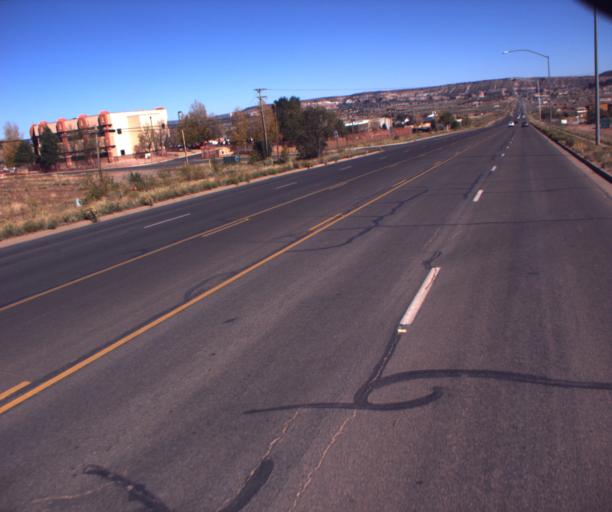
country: US
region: Arizona
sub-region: Apache County
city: Saint Michaels
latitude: 35.6557
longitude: -109.0969
